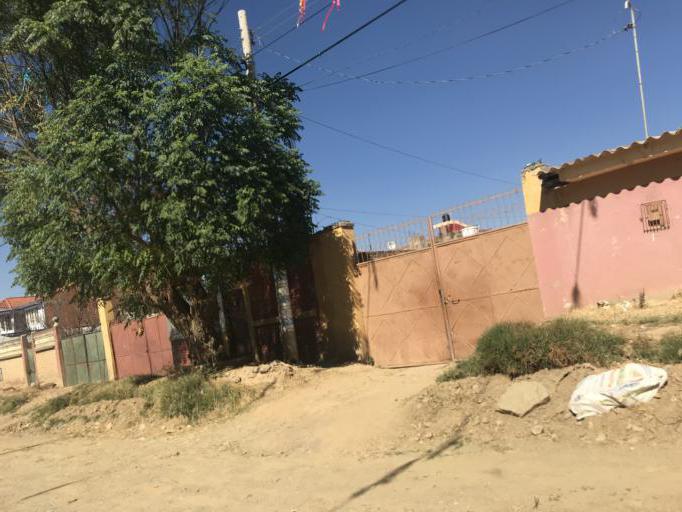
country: BO
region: Cochabamba
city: Cliza
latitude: -17.5883
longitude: -65.9243
